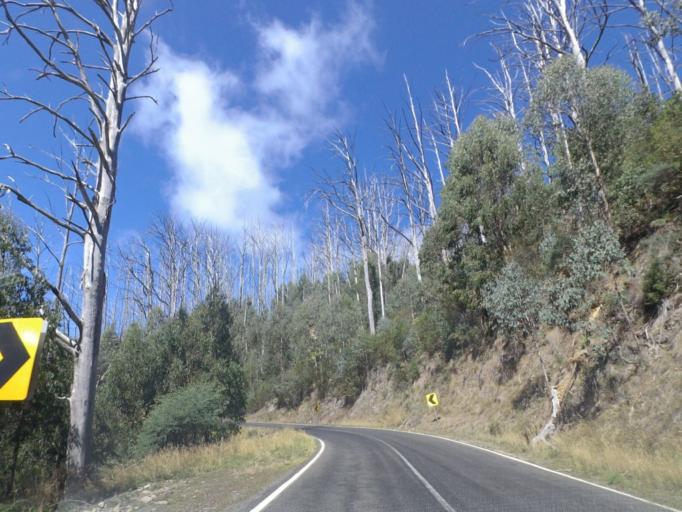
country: AU
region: Victoria
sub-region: Yarra Ranges
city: Millgrove
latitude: -37.5287
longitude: 145.8203
